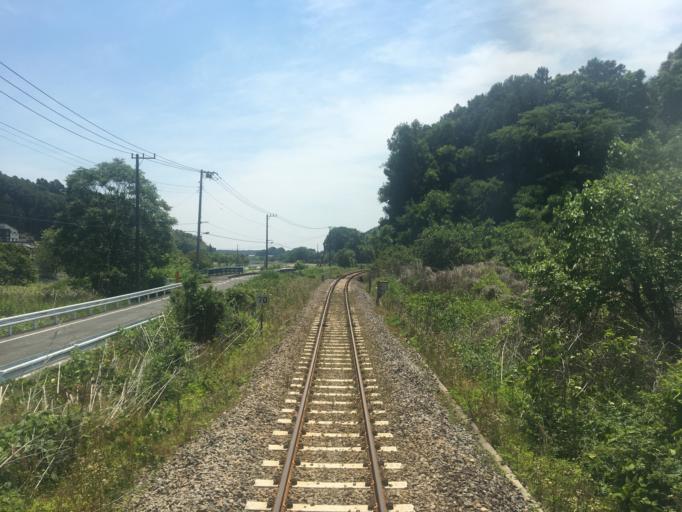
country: JP
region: Saitama
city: Ogawa
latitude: 36.0170
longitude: 139.2784
